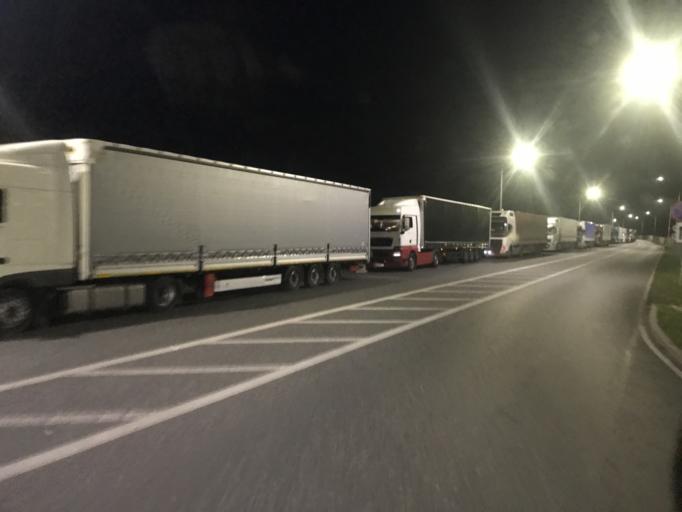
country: PL
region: Lublin Voivodeship
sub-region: Powiat bialski
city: Terespol
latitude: 52.0792
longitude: 23.5235
